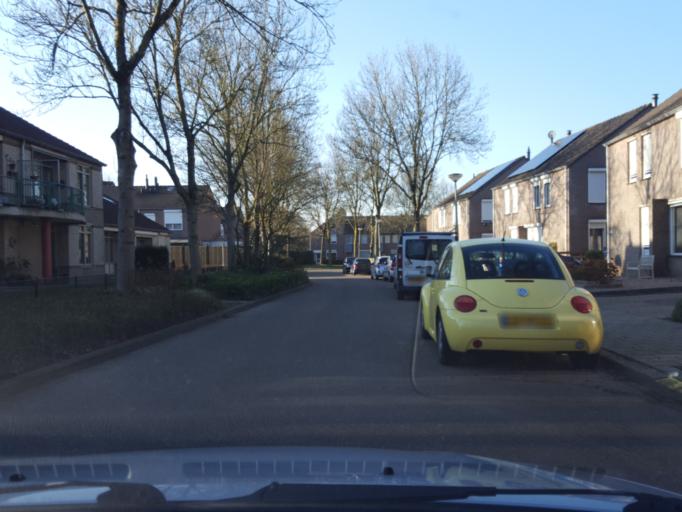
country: NL
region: Limburg
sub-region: Gemeente Sittard-Geleen
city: Limbricht
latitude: 50.9772
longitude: 5.8334
